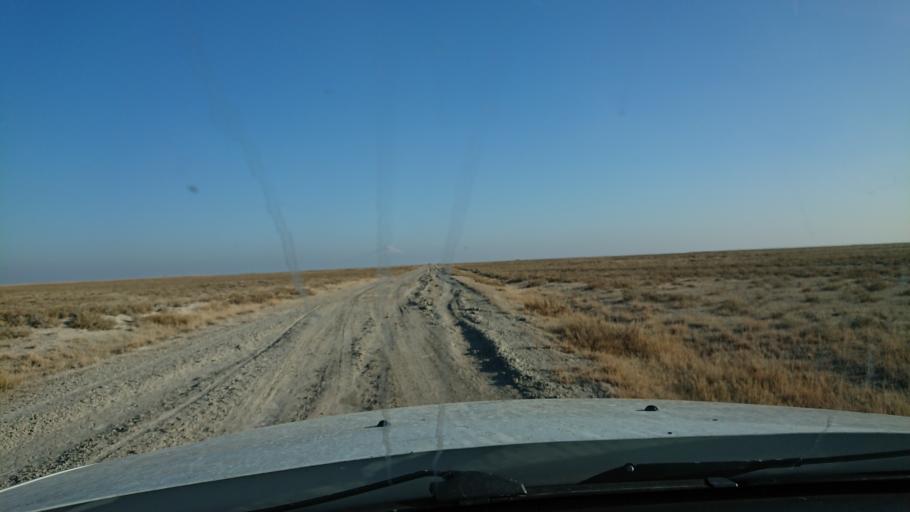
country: TR
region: Aksaray
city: Eskil
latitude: 38.4058
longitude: 33.5718
